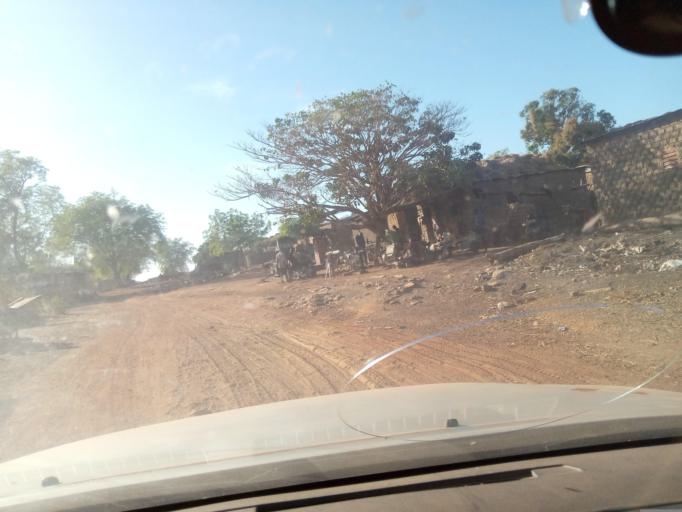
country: ML
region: Sikasso
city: Sikasso
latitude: 11.4861
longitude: -5.4811
